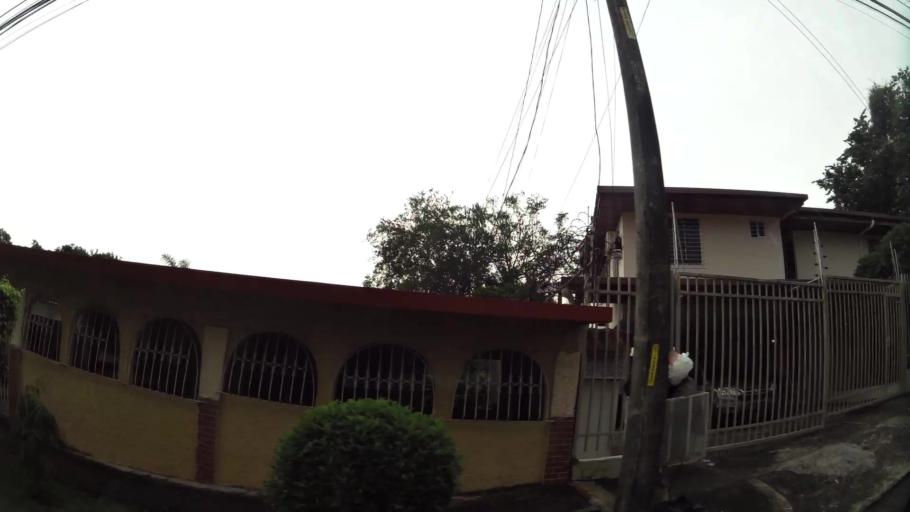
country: PA
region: Panama
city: Panama
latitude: 9.0141
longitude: -79.5248
